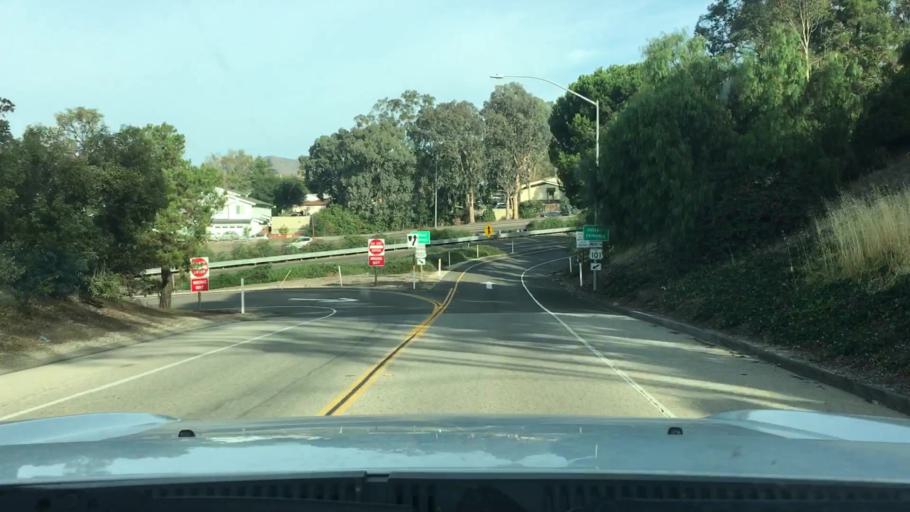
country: US
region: California
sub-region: San Luis Obispo County
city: San Luis Obispo
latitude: 35.2898
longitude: -120.6580
